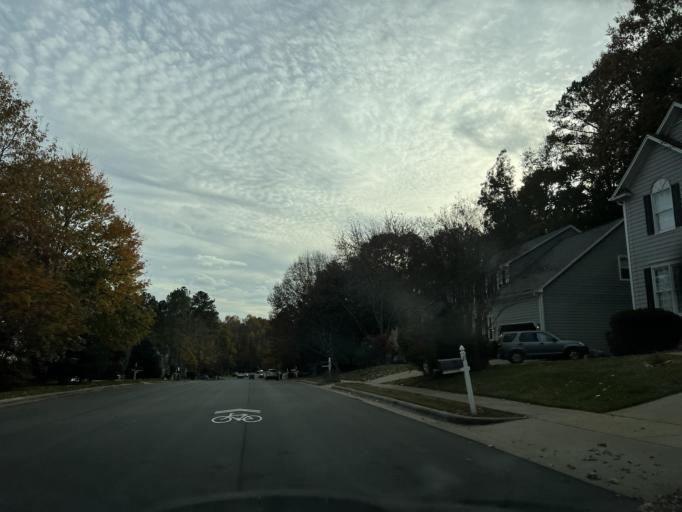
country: US
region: North Carolina
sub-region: Wake County
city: Wake Forest
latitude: 35.9005
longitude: -78.5868
